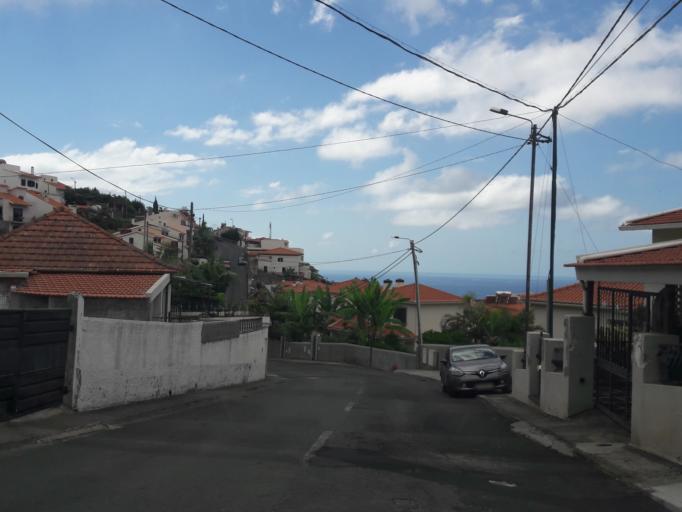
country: PT
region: Madeira
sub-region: Funchal
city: Nossa Senhora do Monte
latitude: 32.6665
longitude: -16.9274
